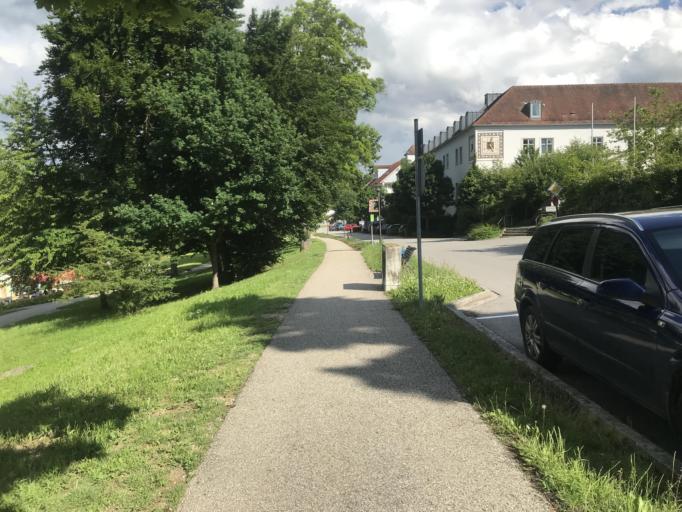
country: DE
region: Bavaria
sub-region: Lower Bavaria
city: Viechtach
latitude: 49.0772
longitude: 12.8905
